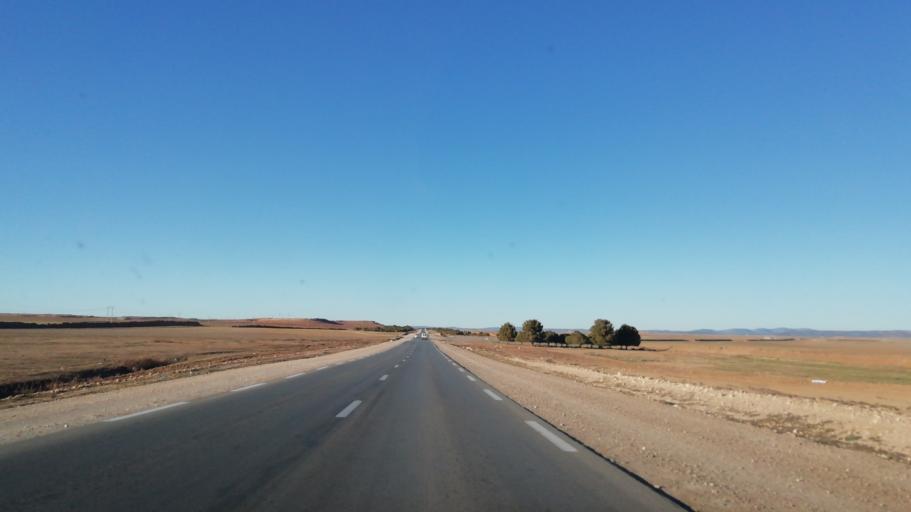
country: DZ
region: Tlemcen
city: Sebdou
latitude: 34.4884
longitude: -1.2732
